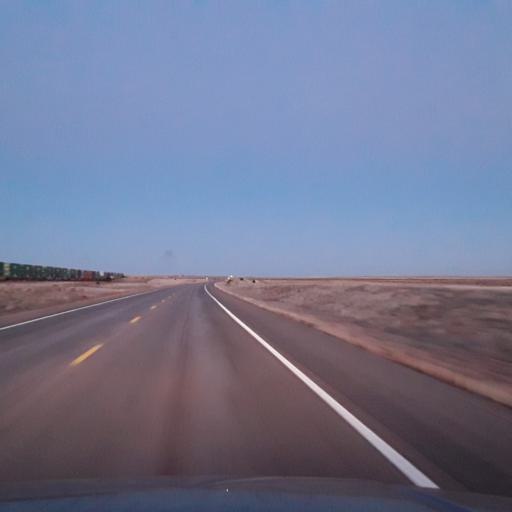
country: US
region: New Mexico
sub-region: Guadalupe County
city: Santa Rosa
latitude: 34.7535
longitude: -105.0048
